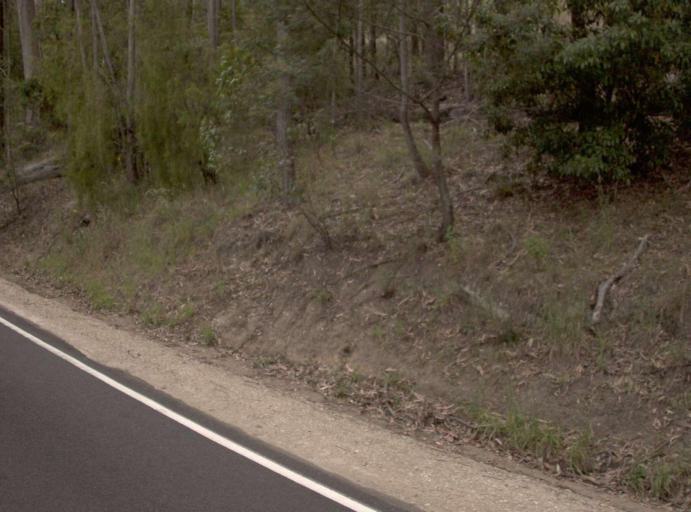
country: AU
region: New South Wales
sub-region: Bombala
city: Bombala
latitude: -37.4544
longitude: 149.1911
